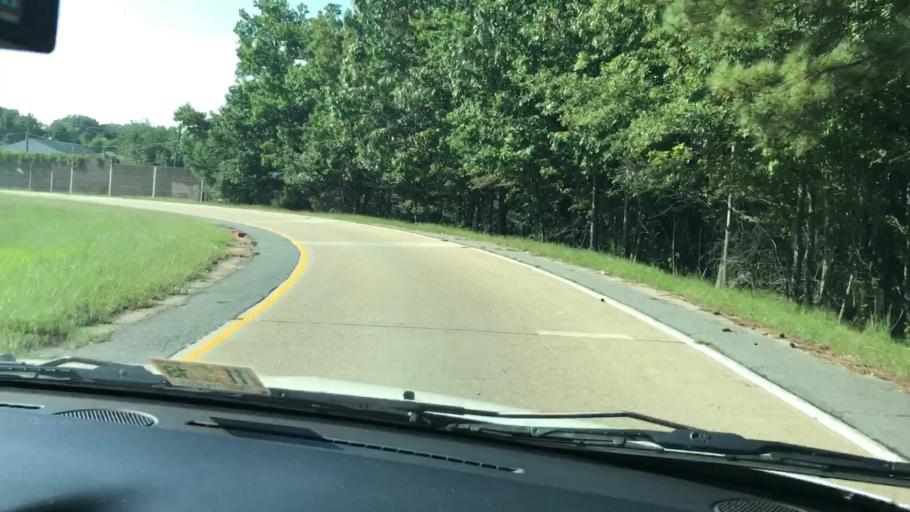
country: US
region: Virginia
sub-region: City of Norfolk
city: Norfolk
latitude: 36.8927
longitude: -76.2299
